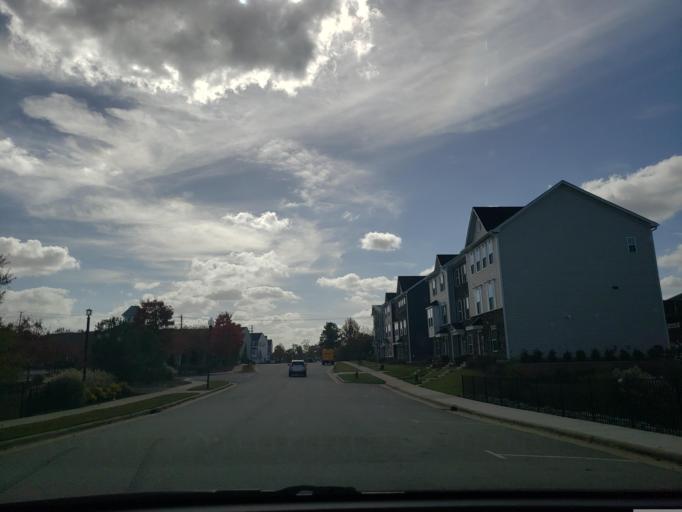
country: US
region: North Carolina
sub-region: Wake County
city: Apex
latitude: 35.7426
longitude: -78.8465
